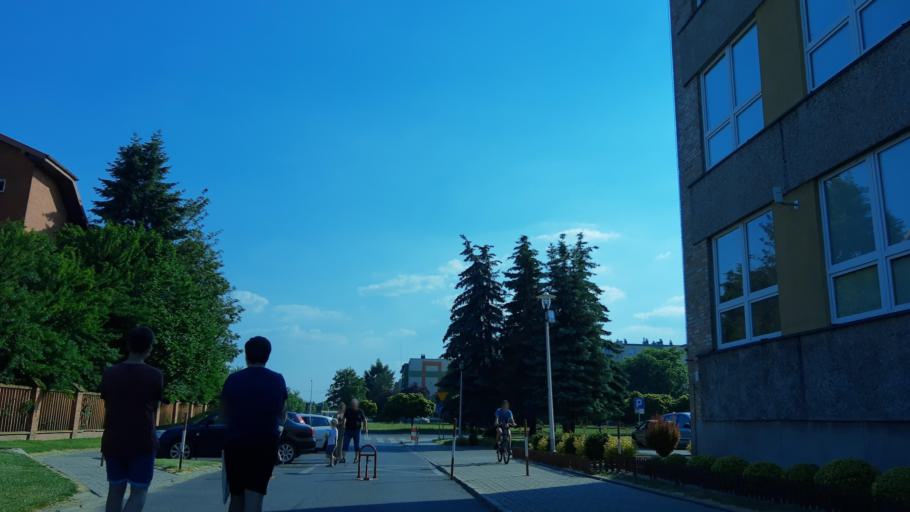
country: PL
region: Lodz Voivodeship
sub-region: Powiat sieradzki
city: Sieradz
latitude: 51.5907
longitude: 18.7171
